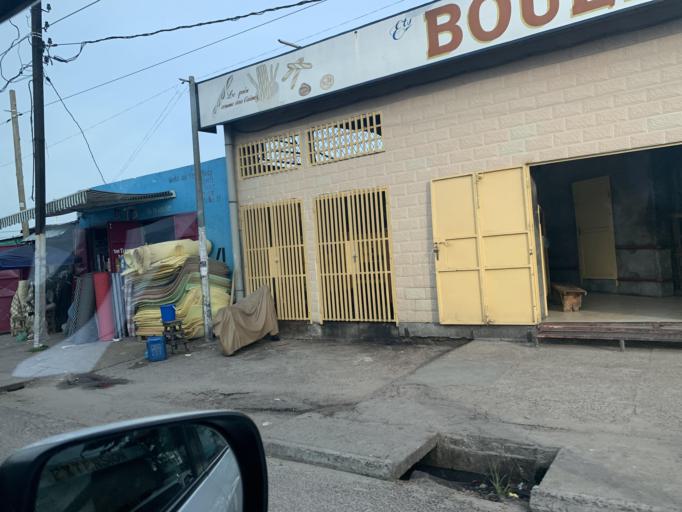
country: CG
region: Brazzaville
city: Brazzaville
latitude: -4.2474
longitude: 15.2821
